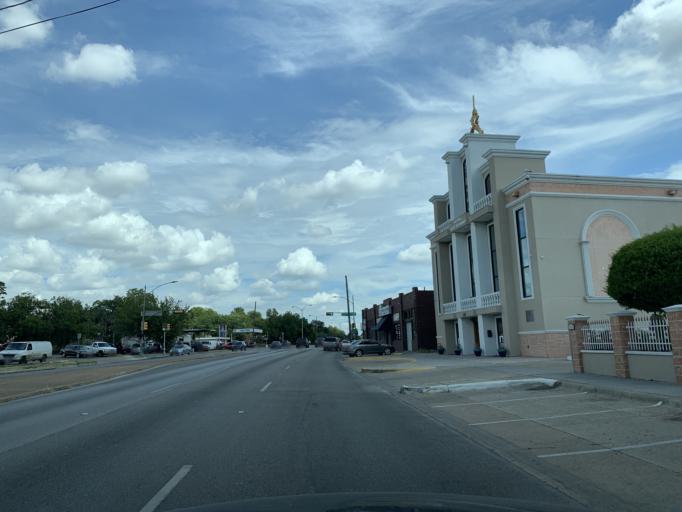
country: US
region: Texas
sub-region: Dallas County
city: Cockrell Hill
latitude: 32.7466
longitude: -96.8523
